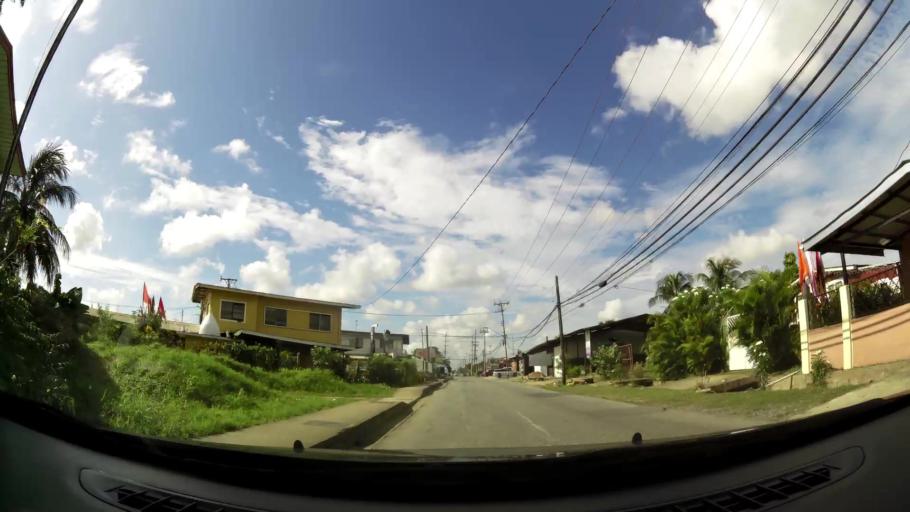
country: TT
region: Chaguanas
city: Chaguanas
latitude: 10.5364
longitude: -61.3990
